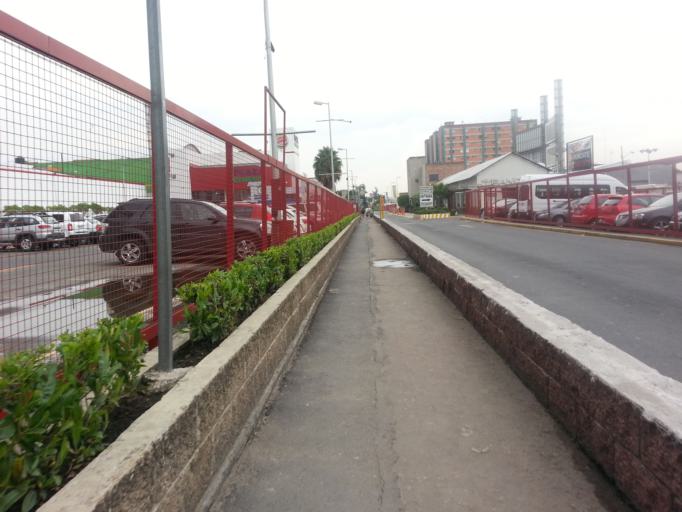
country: MX
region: Mexico City
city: Colonia del Valle
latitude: 19.3874
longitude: -99.1912
